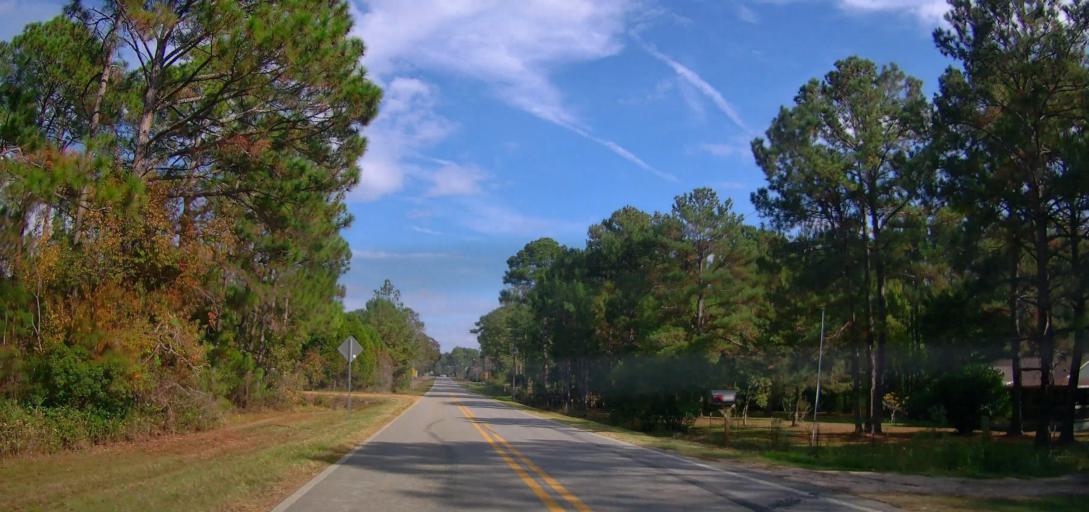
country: US
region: Georgia
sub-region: Thomas County
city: Thomasville
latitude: 30.9497
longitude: -84.0287
